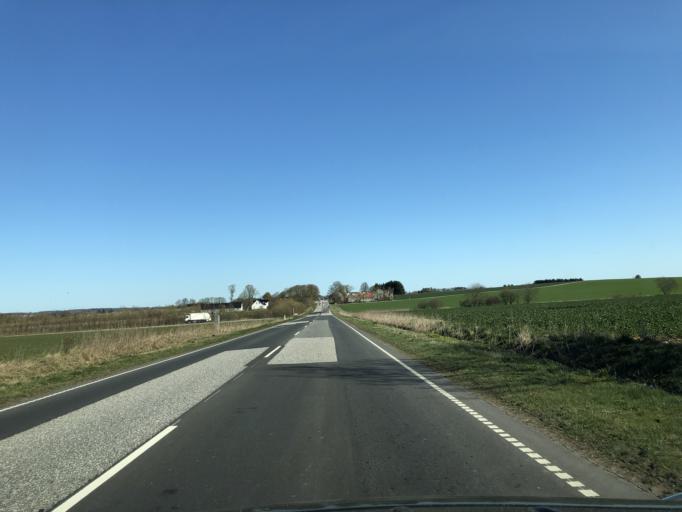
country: DK
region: North Denmark
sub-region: Rebild Kommune
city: Stovring
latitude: 56.8571
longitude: 9.8283
